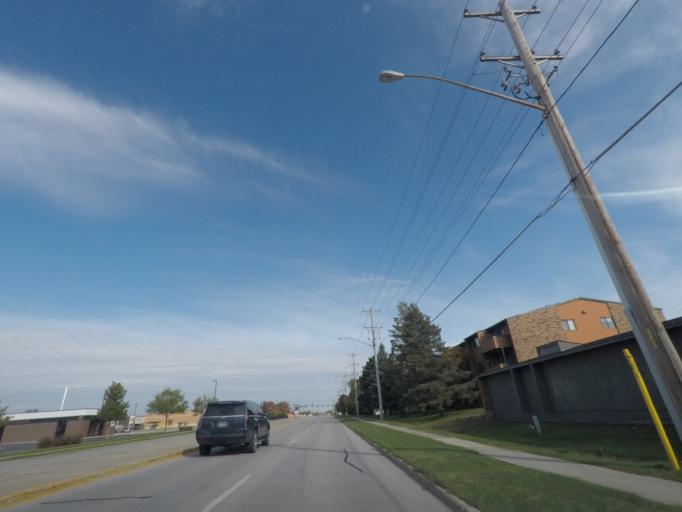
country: US
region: Iowa
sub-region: Story County
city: Ames
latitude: 42.0471
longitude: -93.6204
